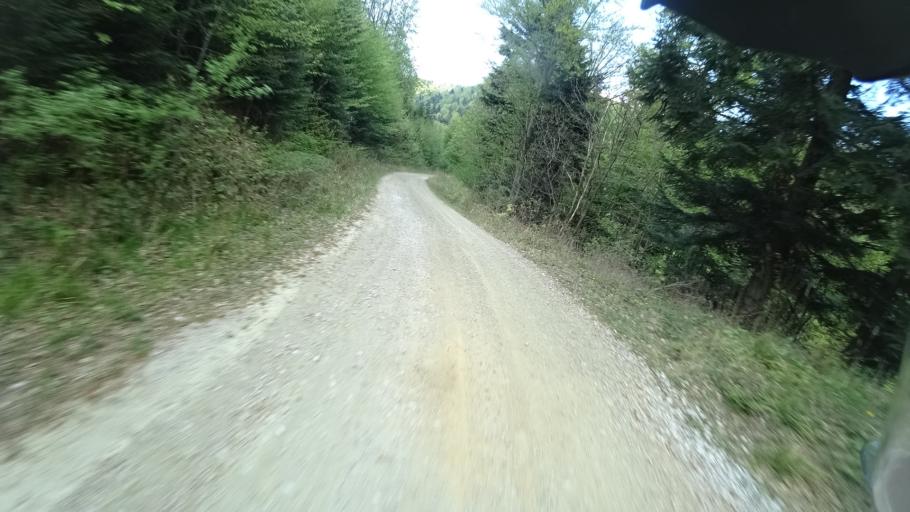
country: HR
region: Grad Zagreb
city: Kasina
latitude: 45.9142
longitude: 15.9986
